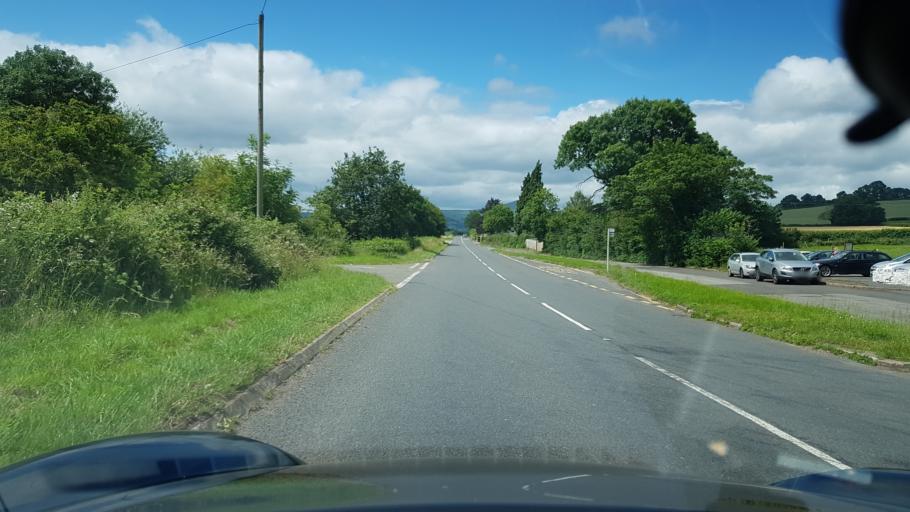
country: GB
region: Wales
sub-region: Monmouthshire
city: Abergavenny
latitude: 51.7970
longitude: -2.9951
